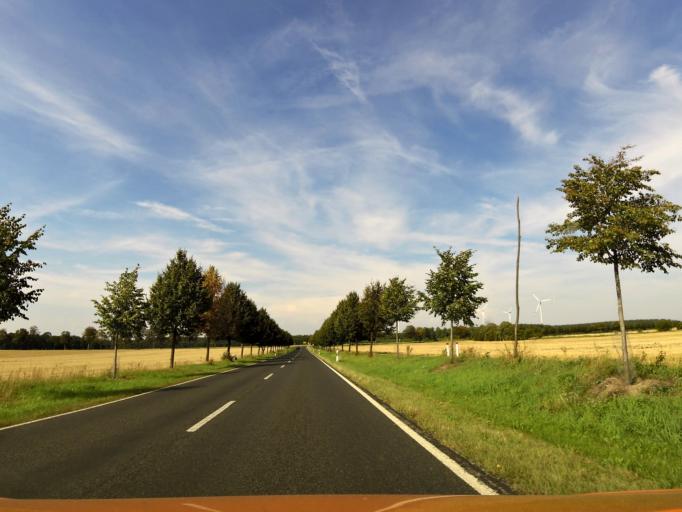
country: DE
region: Brandenburg
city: Ludwigsfelde
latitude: 52.3365
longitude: 13.2514
